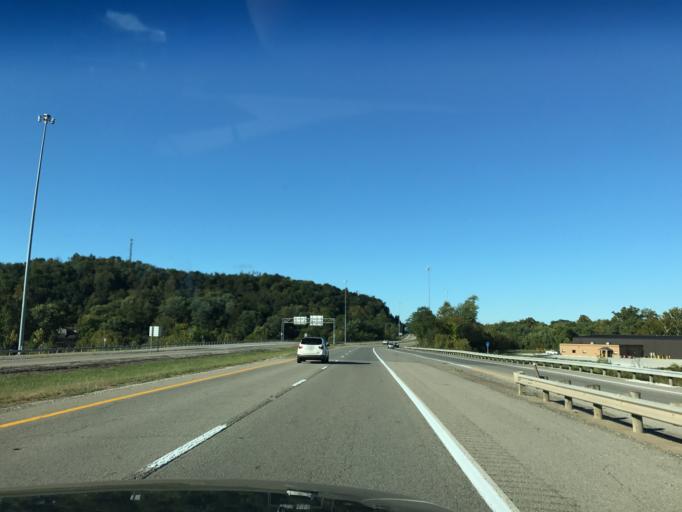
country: US
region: West Virginia
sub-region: Wood County
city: Parkersburg
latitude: 39.2657
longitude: -81.5136
